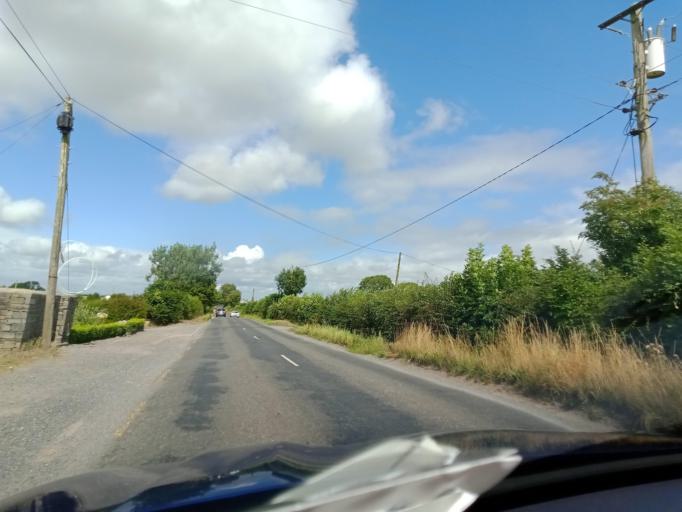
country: IE
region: Leinster
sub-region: Laois
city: Portlaoise
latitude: 52.9611
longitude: -7.2978
